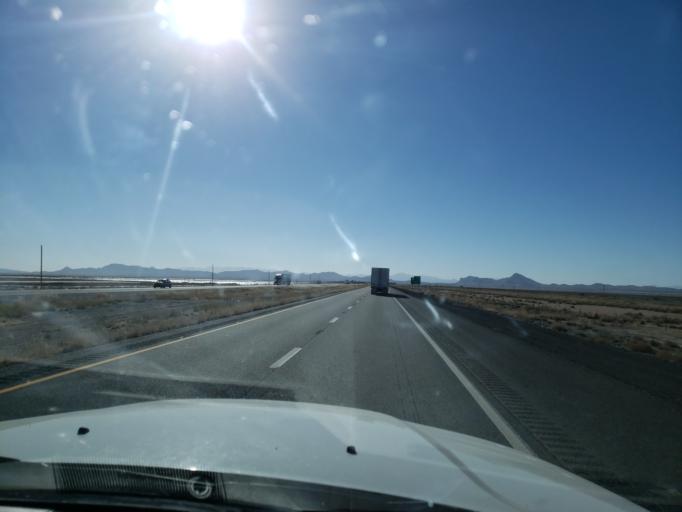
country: US
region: New Mexico
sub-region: Hidalgo County
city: Lordsburg
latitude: 32.2910
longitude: -108.8619
